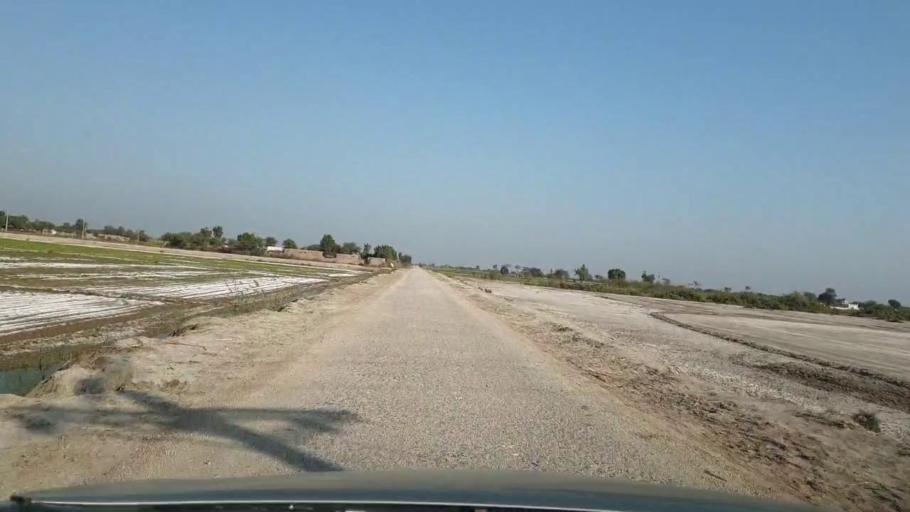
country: PK
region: Sindh
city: Tando Allahyar
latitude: 25.5937
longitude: 68.6301
